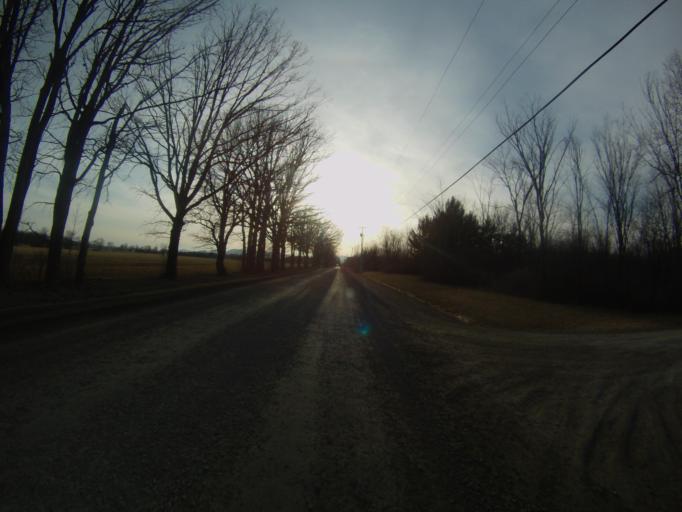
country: US
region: New York
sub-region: Essex County
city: Port Henry
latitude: 44.0274
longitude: -73.3342
